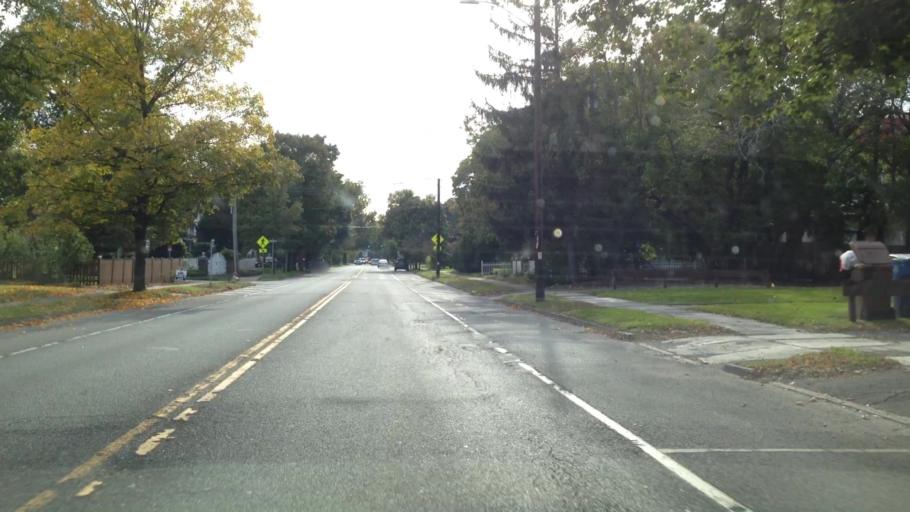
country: US
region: New York
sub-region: Ulster County
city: Kingston
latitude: 41.9365
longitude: -74.0051
